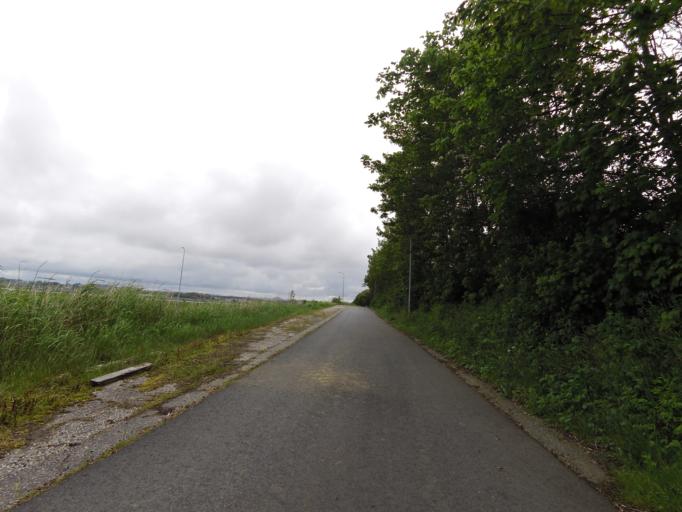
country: NO
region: Rogaland
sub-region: Klepp
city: Kleppe
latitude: 58.8199
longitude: 5.5880
